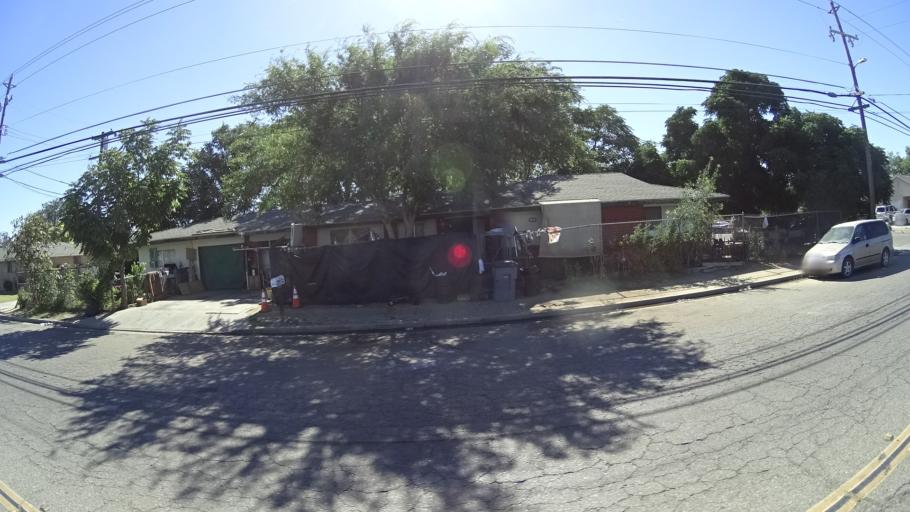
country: US
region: California
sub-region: Fresno County
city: West Park
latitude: 36.7090
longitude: -119.8089
